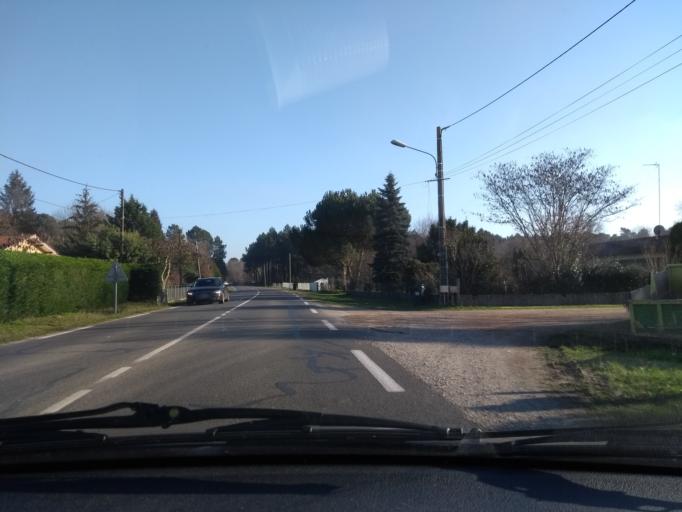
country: FR
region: Aquitaine
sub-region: Departement de la Gironde
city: Mios
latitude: 44.5951
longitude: -0.9064
